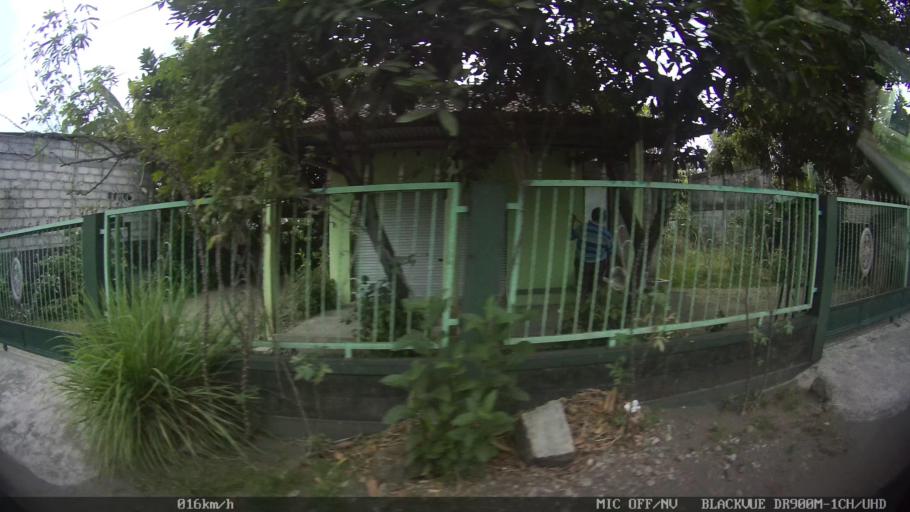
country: ID
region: Daerah Istimewa Yogyakarta
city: Sewon
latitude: -7.8705
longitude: 110.4075
